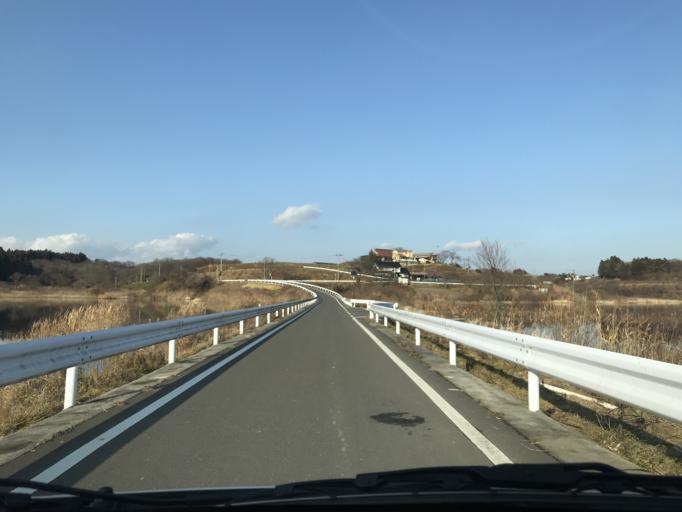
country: JP
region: Miyagi
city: Wakuya
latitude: 38.6884
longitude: 141.1064
